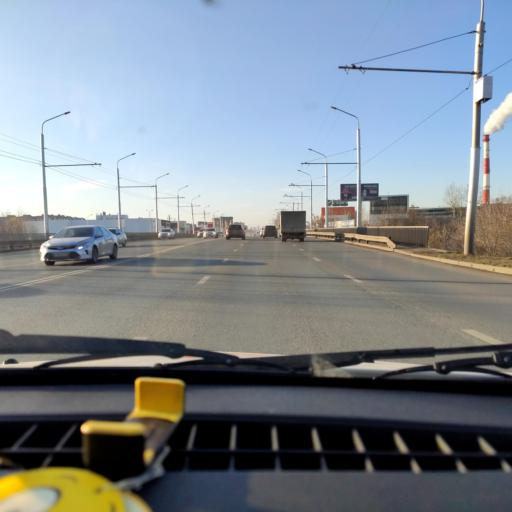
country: RU
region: Bashkortostan
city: Ufa
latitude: 54.7866
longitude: 56.0771
